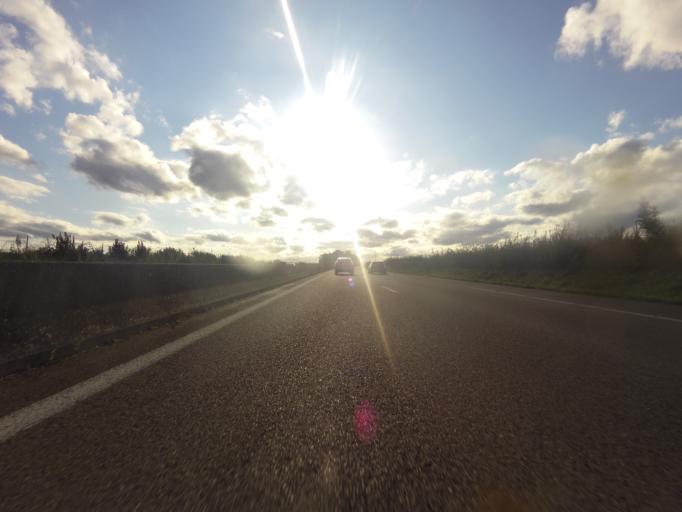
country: FR
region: Picardie
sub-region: Departement de la Somme
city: Poix-de-Picardie
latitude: 49.8149
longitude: 2.0255
